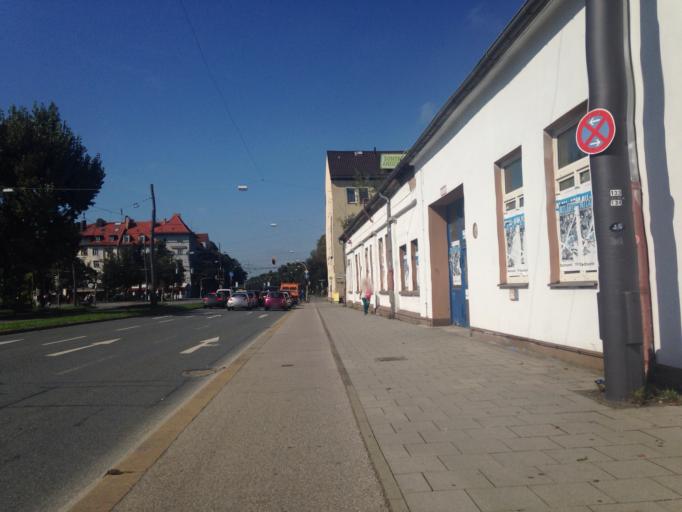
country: DE
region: Bavaria
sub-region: Upper Bavaria
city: Munich
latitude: 48.1588
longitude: 11.5484
